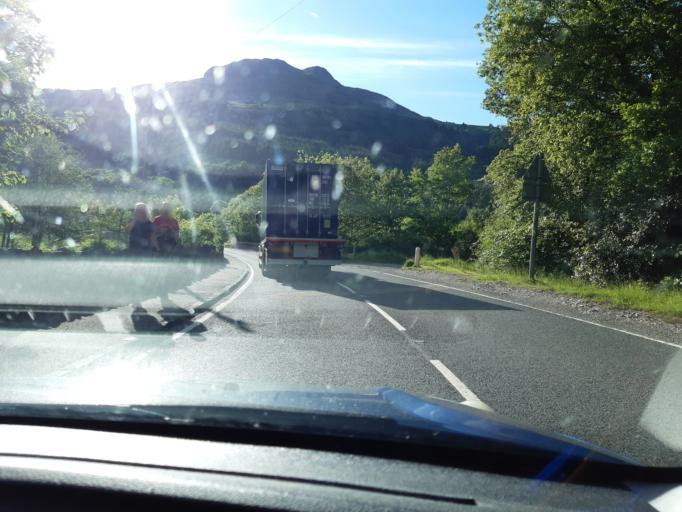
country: GB
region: Scotland
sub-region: Argyll and Bute
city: Garelochhead
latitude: 56.2069
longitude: -4.7449
